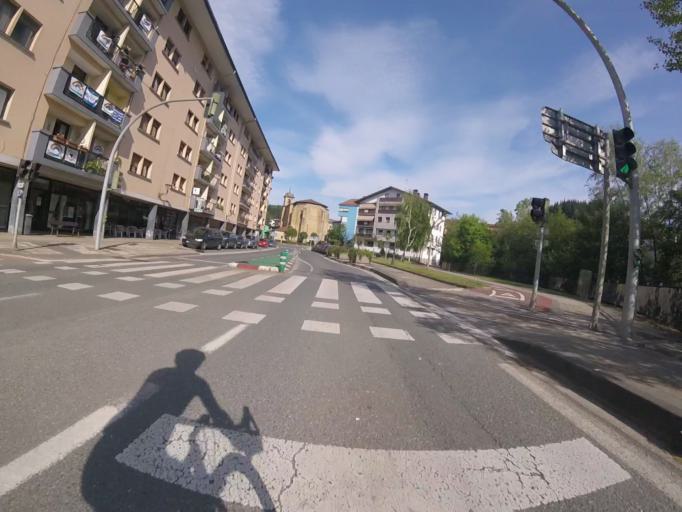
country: ES
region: Basque Country
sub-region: Provincia de Guipuzcoa
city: Ormaiztegui
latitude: 43.0427
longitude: -2.2525
